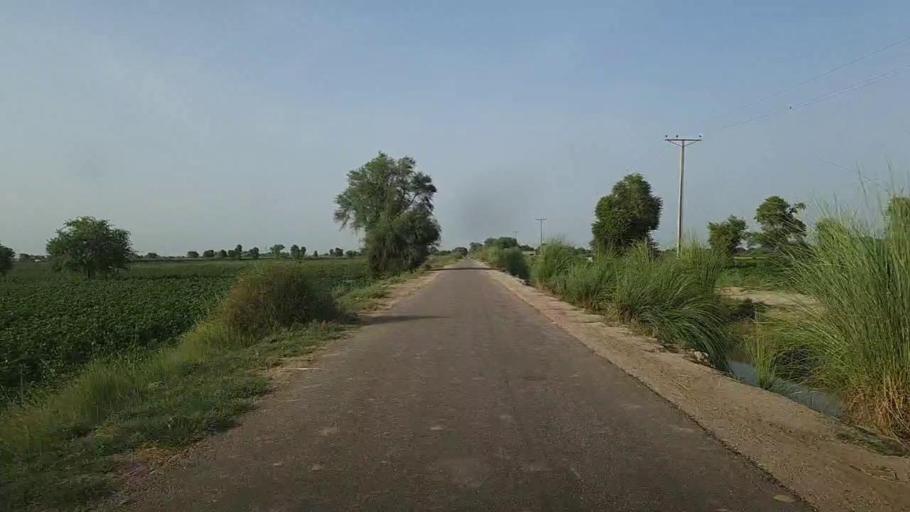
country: PK
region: Sindh
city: Ubauro
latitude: 28.0909
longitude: 69.8194
